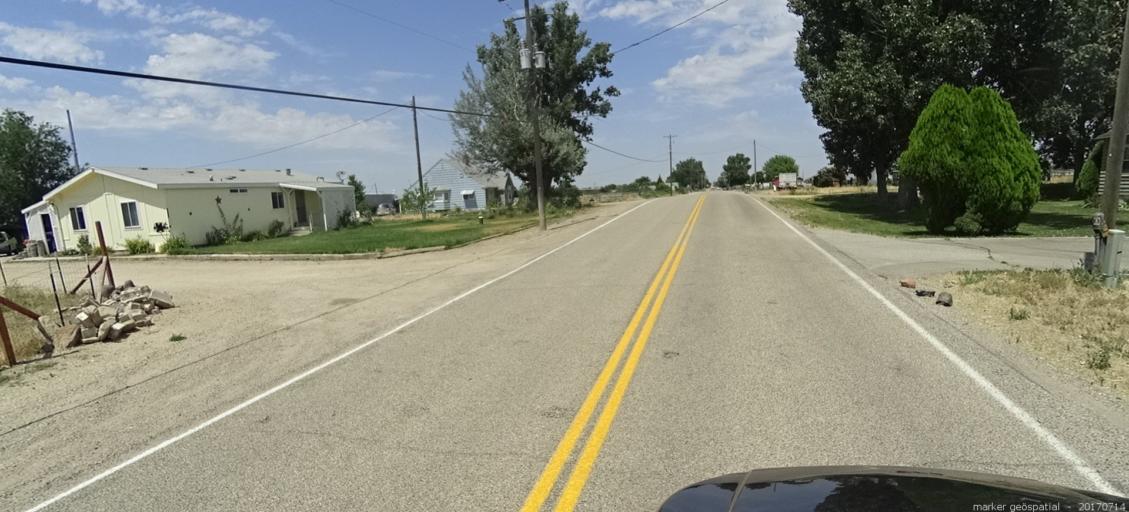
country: US
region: Idaho
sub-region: Ada County
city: Kuna
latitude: 43.5277
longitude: -116.3543
